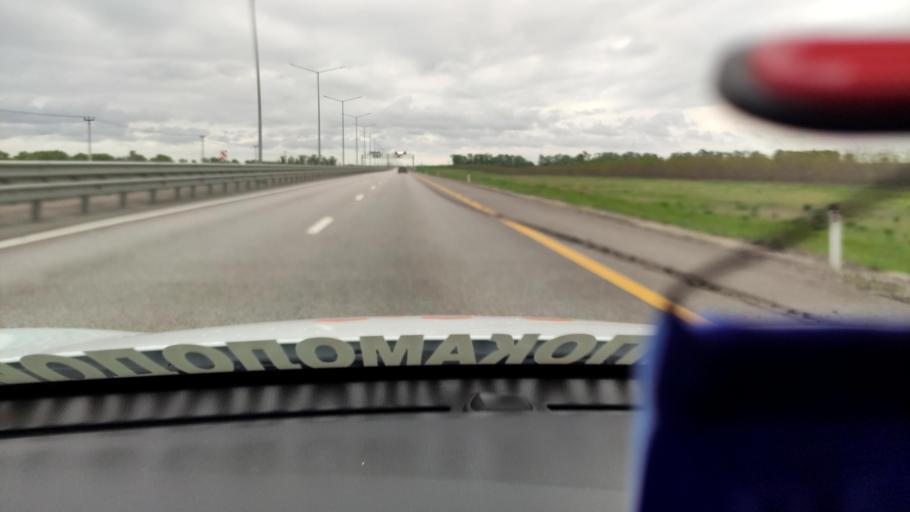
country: RU
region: Voronezj
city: Podkletnoye
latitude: 51.5676
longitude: 39.4749
